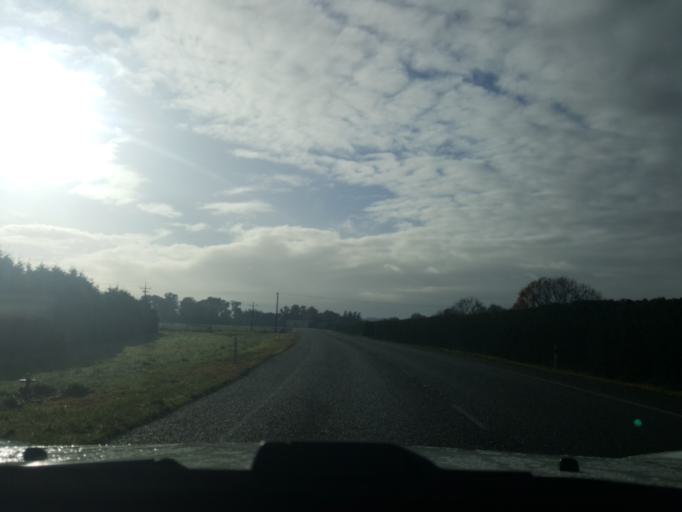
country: NZ
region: Waikato
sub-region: Waipa District
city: Cambridge
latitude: -37.7802
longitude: 175.3958
